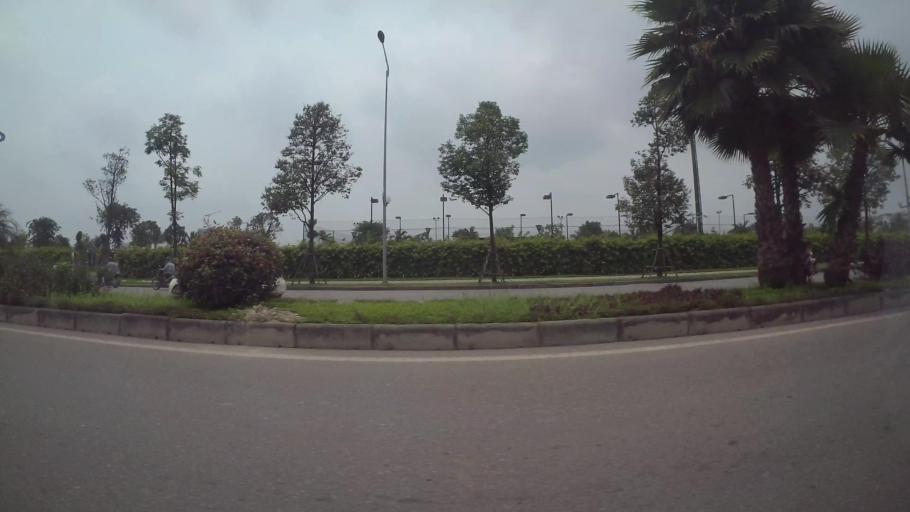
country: VN
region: Ha Noi
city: Trau Quy
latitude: 21.0492
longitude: 105.9089
